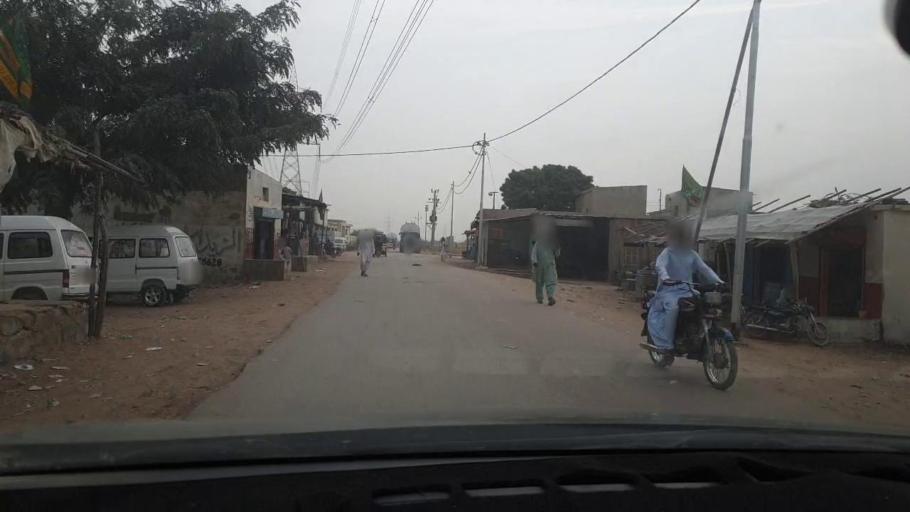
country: PK
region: Sindh
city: Malir Cantonment
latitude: 24.9066
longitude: 67.2862
